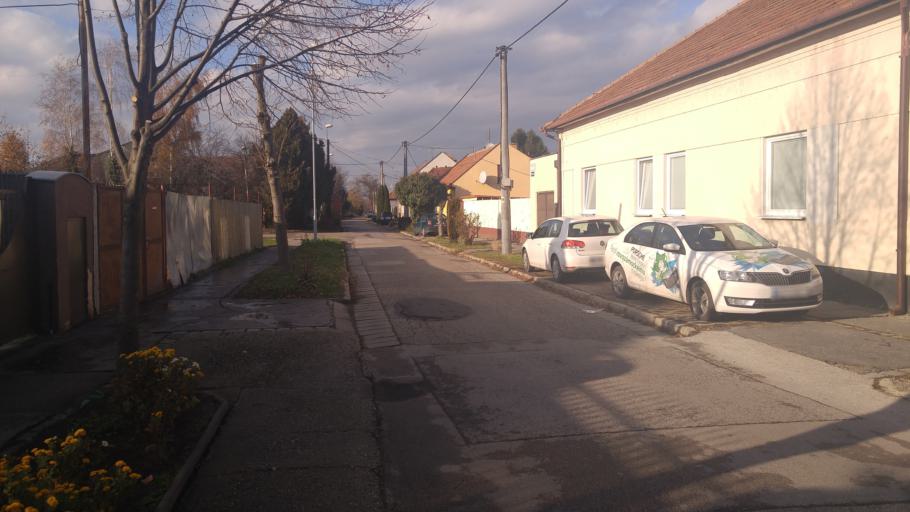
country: SK
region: Nitriansky
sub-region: Okres Nove Zamky
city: Nove Zamky
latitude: 47.9916
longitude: 18.1576
